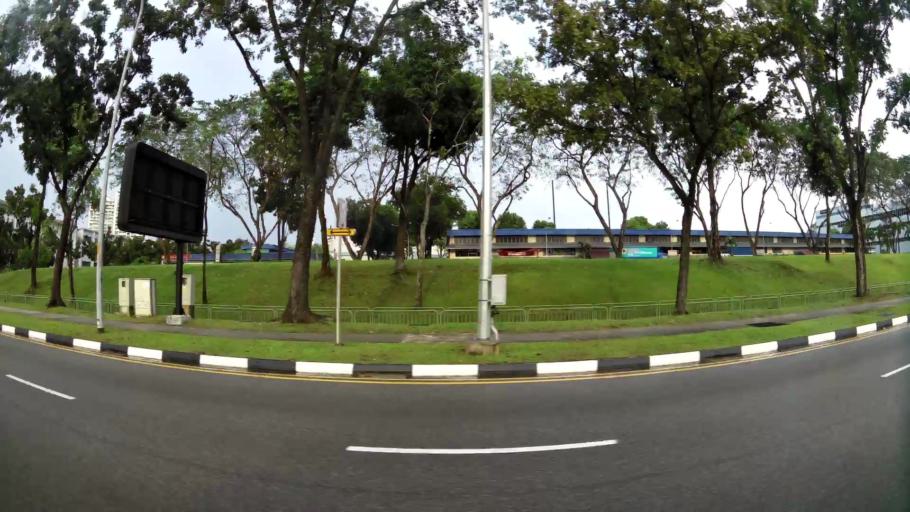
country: SG
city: Singapore
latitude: 1.3578
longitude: 103.8542
